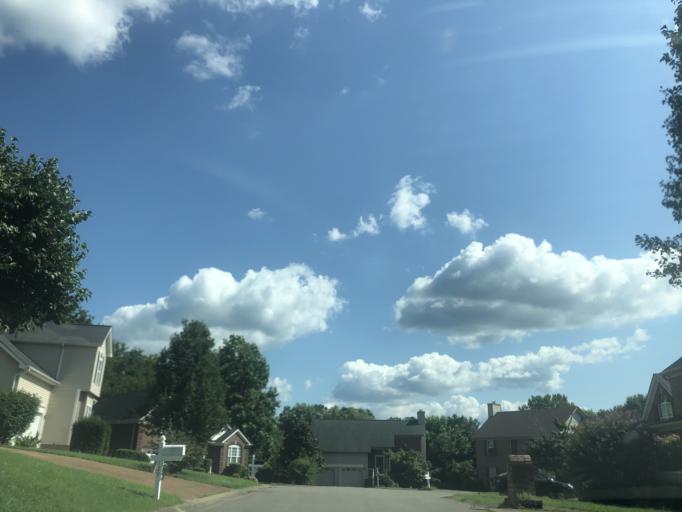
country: US
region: Tennessee
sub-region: Davidson County
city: Lakewood
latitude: 36.1895
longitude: -86.6047
